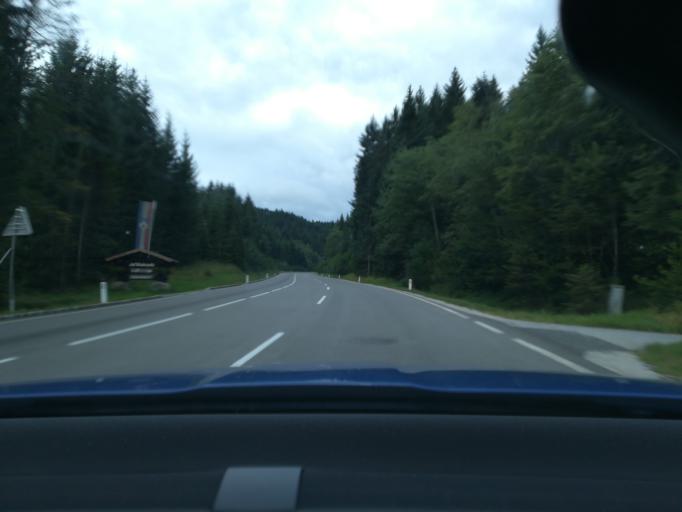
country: AT
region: Upper Austria
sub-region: Politischer Bezirk Gmunden
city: Bad Goisern
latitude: 47.5869
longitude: 13.5223
